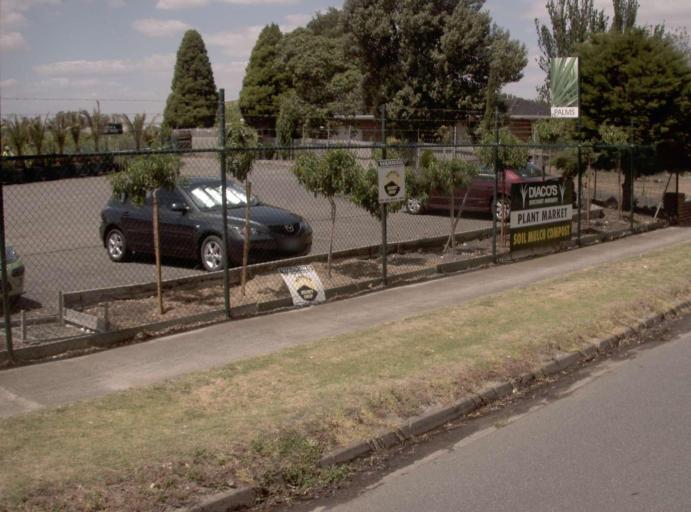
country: AU
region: Victoria
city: Heatherton
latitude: -37.9578
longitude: 145.1009
